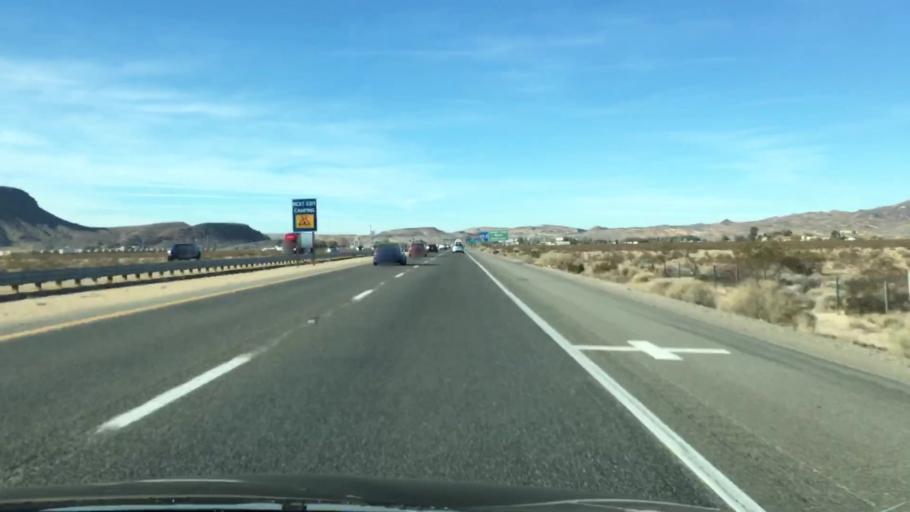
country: US
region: California
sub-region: San Bernardino County
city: Barstow
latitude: 34.9046
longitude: -116.8726
